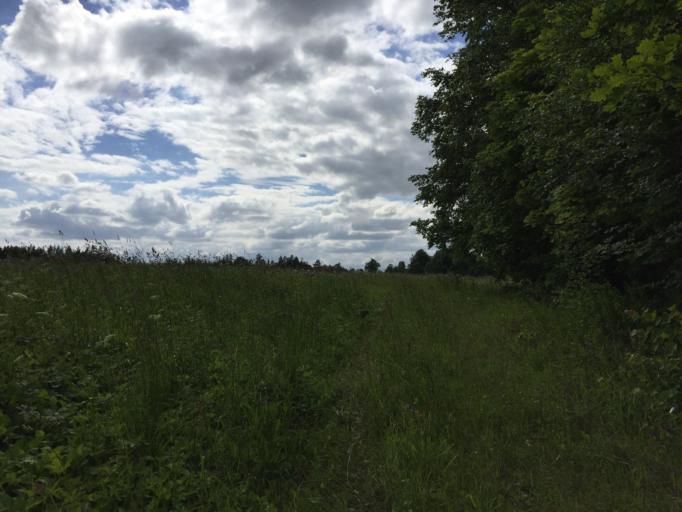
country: LV
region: Apes Novads
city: Ape
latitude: 57.5422
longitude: 26.4533
